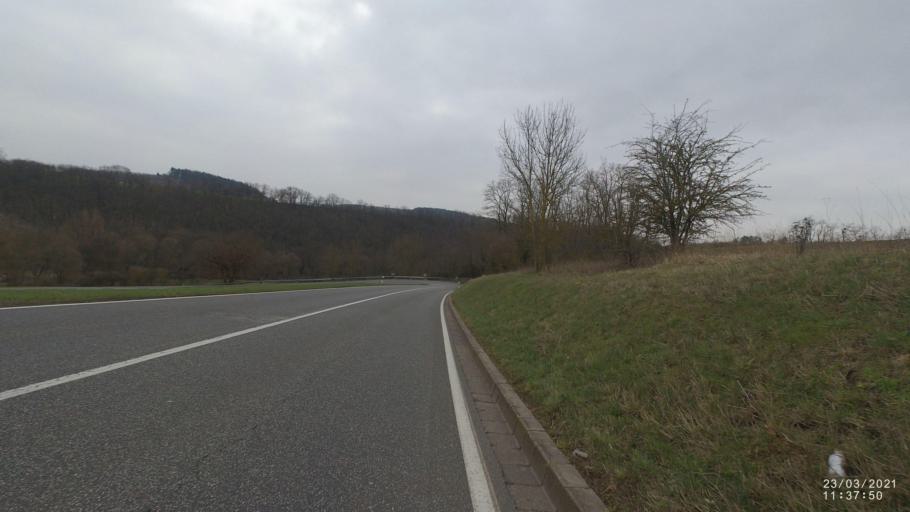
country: DE
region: Rheinland-Pfalz
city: Ochtendung
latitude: 50.3480
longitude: 7.3647
